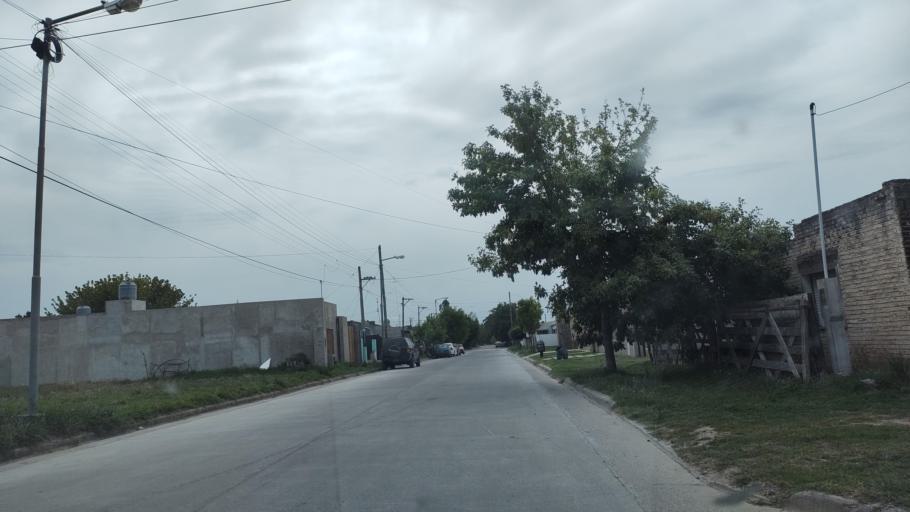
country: AR
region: Buenos Aires
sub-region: Partido de Loberia
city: Loberia
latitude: -38.1620
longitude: -58.7738
